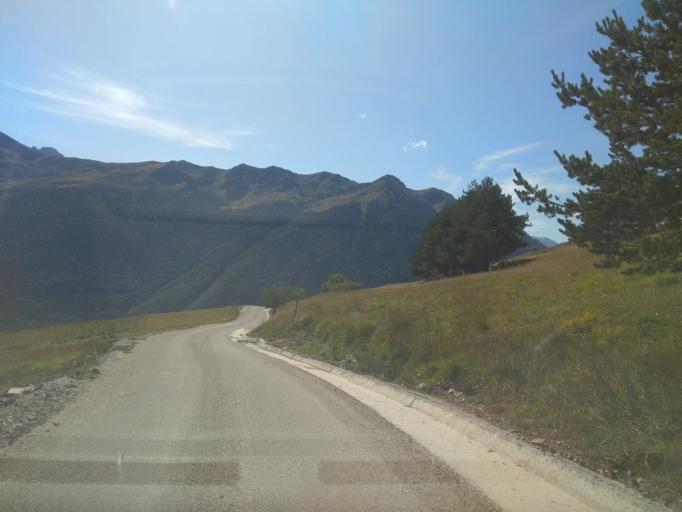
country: ES
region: Catalonia
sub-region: Provincia de Lleida
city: Les
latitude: 42.7638
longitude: 0.7110
